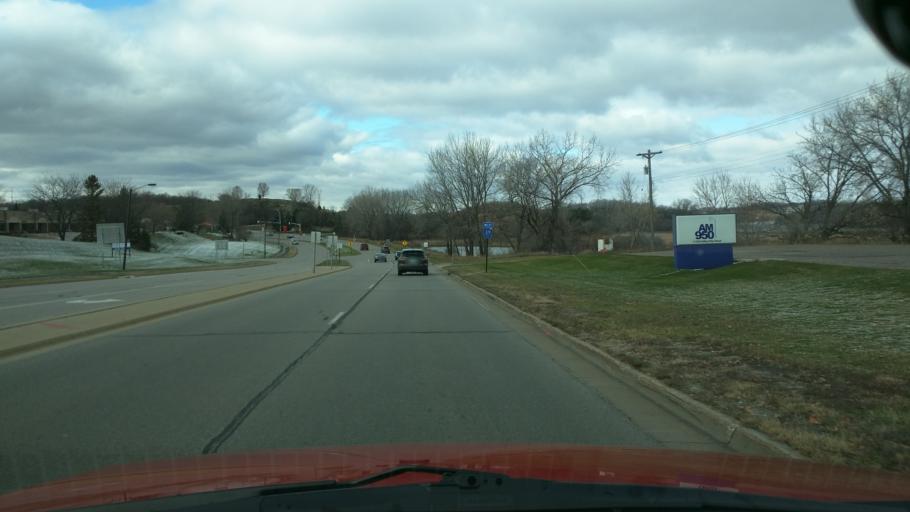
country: US
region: Minnesota
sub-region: Hennepin County
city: Eden Prairie
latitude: 44.8671
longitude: -93.4207
